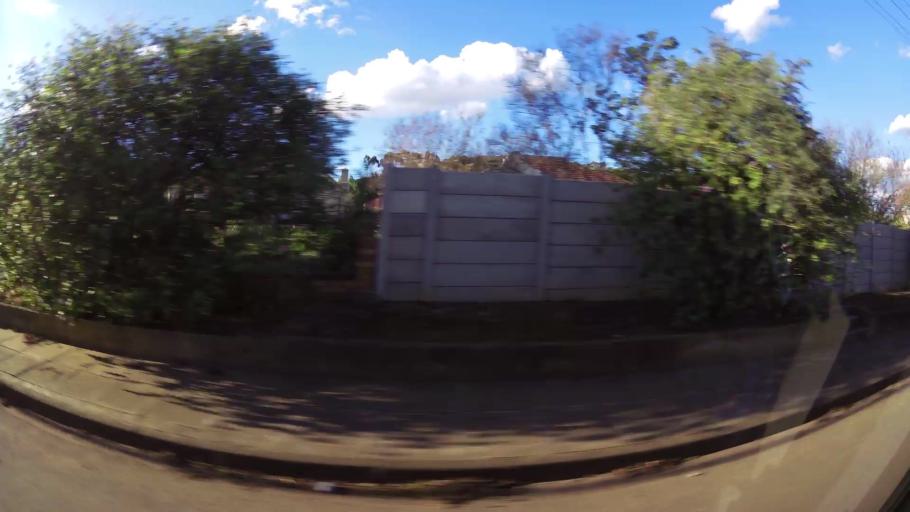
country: ZA
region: Western Cape
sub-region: Eden District Municipality
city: Riversdale
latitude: -34.0850
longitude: 20.9489
